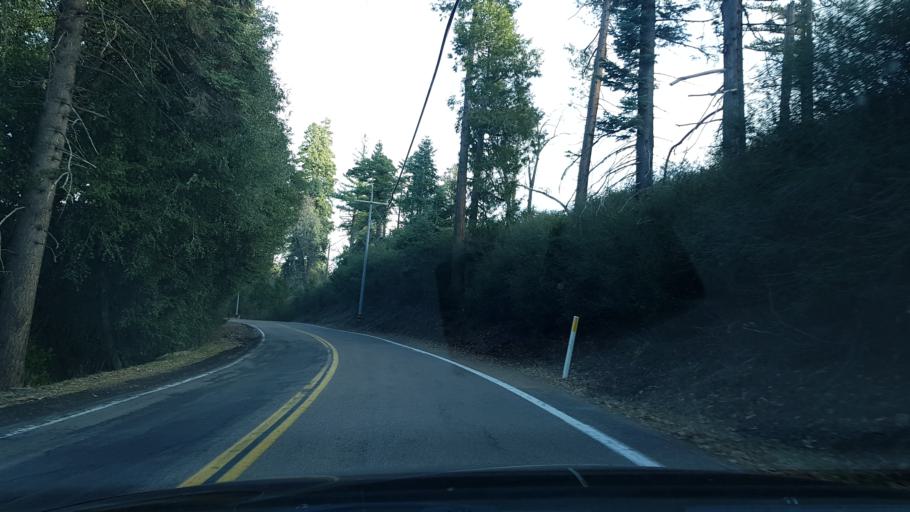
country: US
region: California
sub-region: Riverside County
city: Aguanga
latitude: 33.3279
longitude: -116.8989
